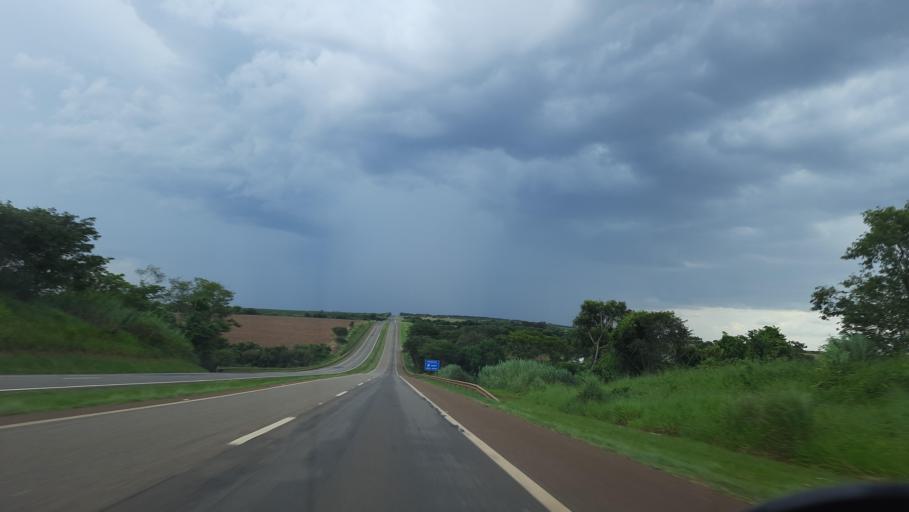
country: BR
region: Sao Paulo
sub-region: Aguai
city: Aguai
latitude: -22.0635
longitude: -47.0250
